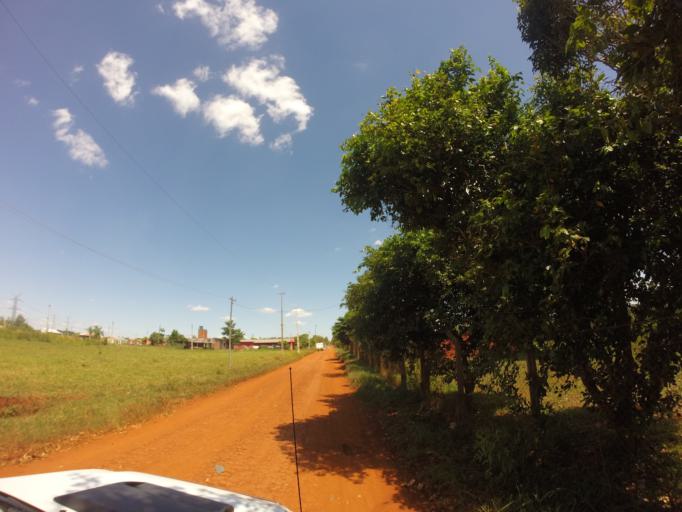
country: PY
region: Alto Parana
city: Ciudad del Este
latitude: -25.4291
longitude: -54.6533
